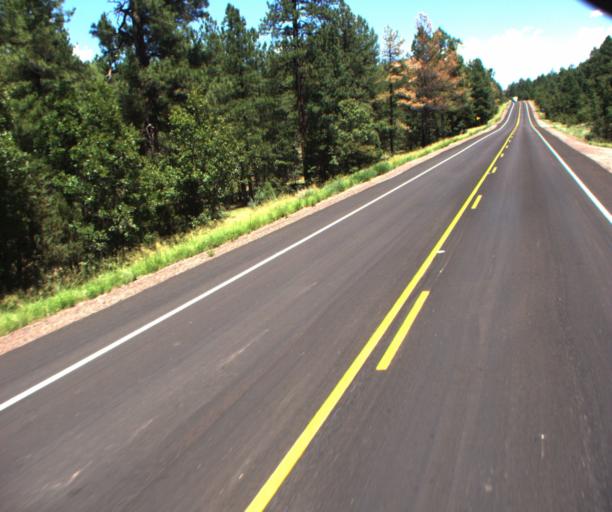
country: US
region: Arizona
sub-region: Navajo County
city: Show Low
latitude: 34.1975
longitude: -110.0869
